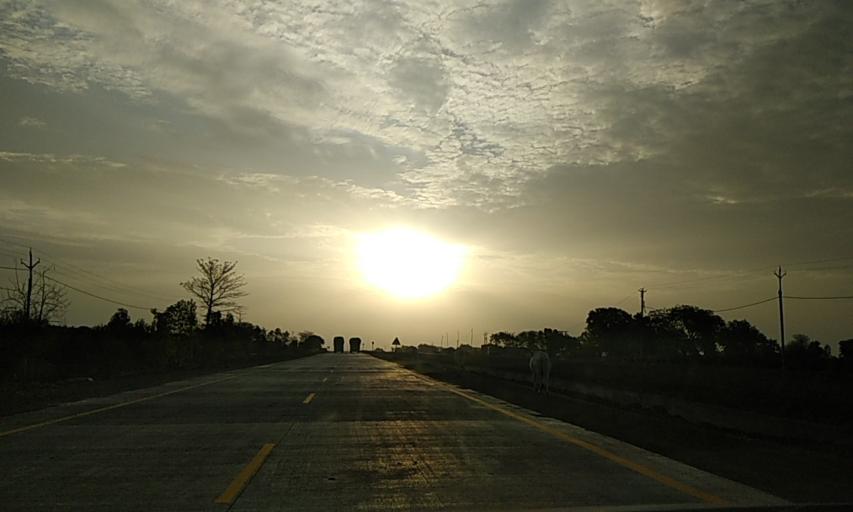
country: IN
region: Madhya Pradesh
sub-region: Rajgarh
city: Khujner
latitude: 23.6861
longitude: 76.6527
